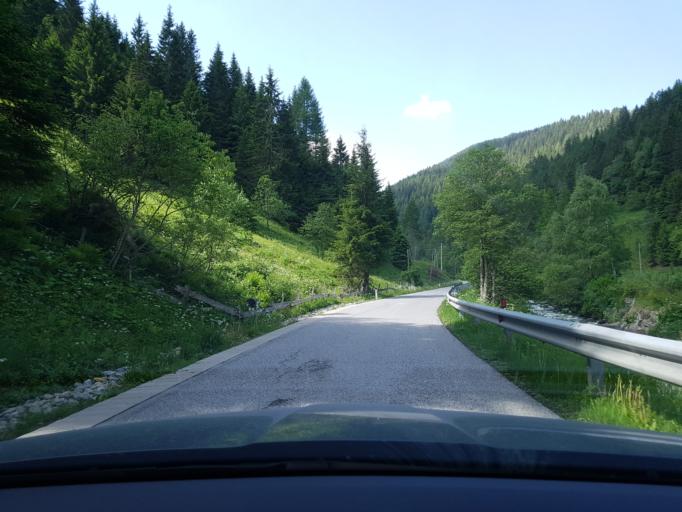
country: AT
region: Salzburg
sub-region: Politischer Bezirk Tamsweg
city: Thomatal
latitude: 47.0524
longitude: 13.7133
